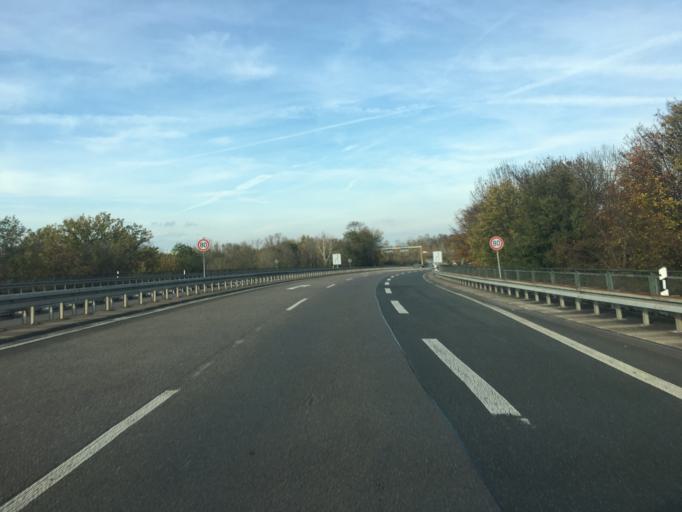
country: DE
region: North Rhine-Westphalia
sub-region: Regierungsbezirk Koln
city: Merheim
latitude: 50.9473
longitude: 7.0577
